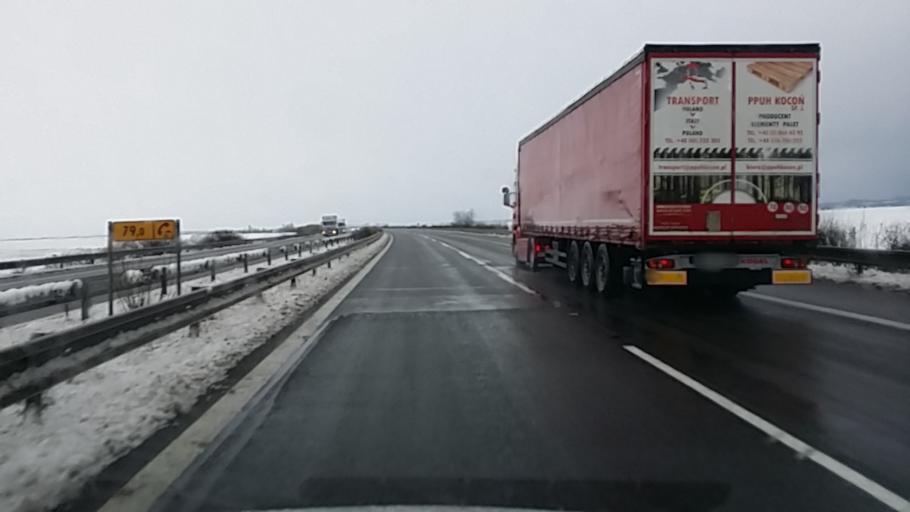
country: HU
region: Gyor-Moson-Sopron
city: Rajka
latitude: 48.0242
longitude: 17.1650
